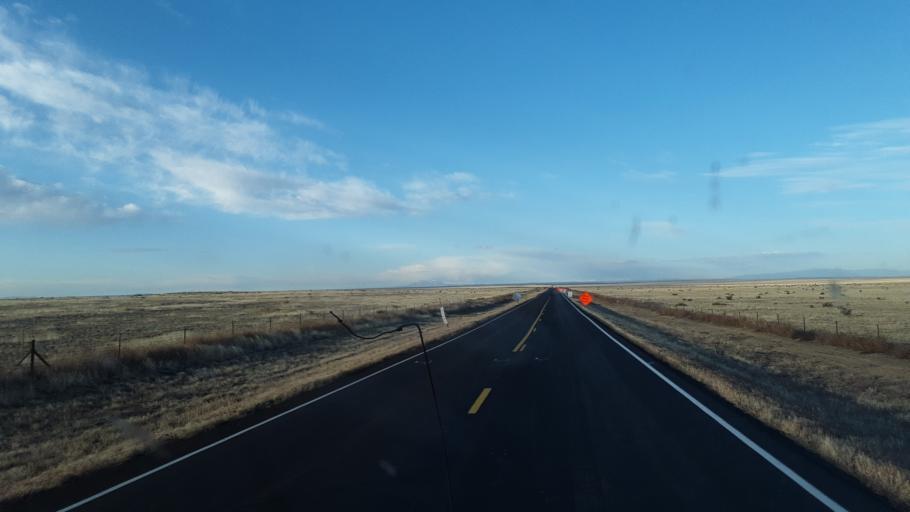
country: US
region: Colorado
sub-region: Otero County
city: Rocky Ford
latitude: 37.9665
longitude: -103.8313
